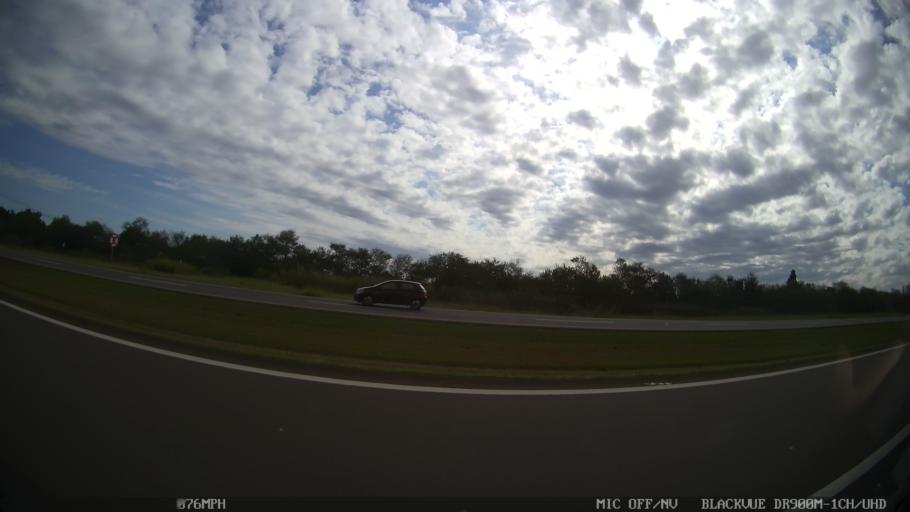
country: BR
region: Sao Paulo
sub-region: Iracemapolis
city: Iracemapolis
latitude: -22.6091
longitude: -47.4599
